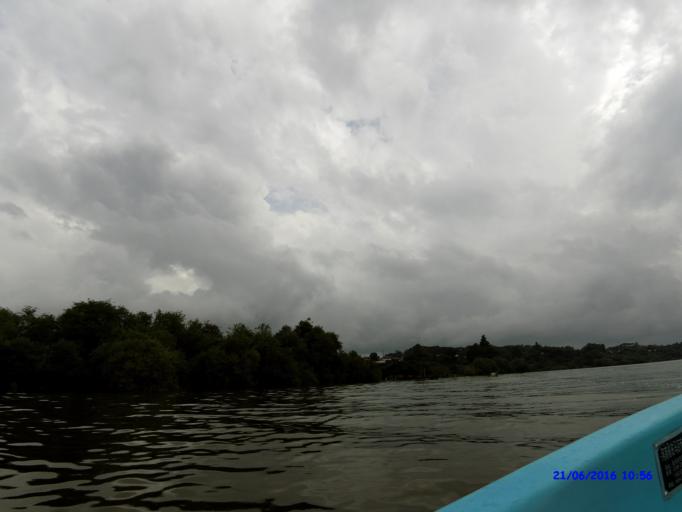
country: BJ
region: Mono
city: Come
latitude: 6.4980
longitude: 1.9598
